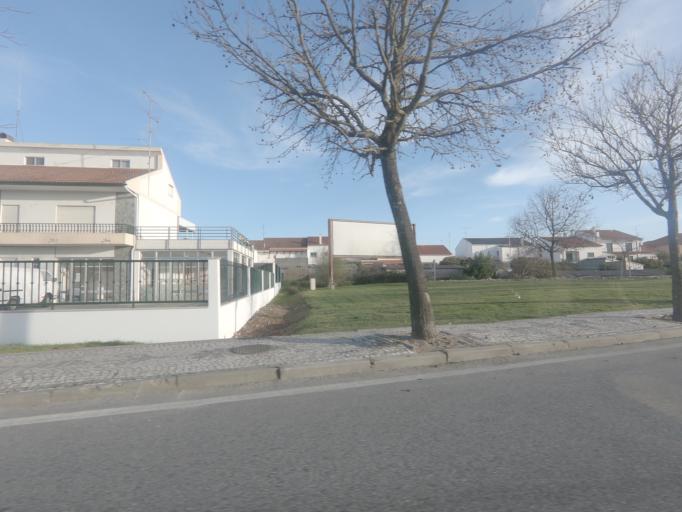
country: PT
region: Castelo Branco
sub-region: Castelo Branco
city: Castelo Branco
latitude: 39.8134
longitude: -7.5052
